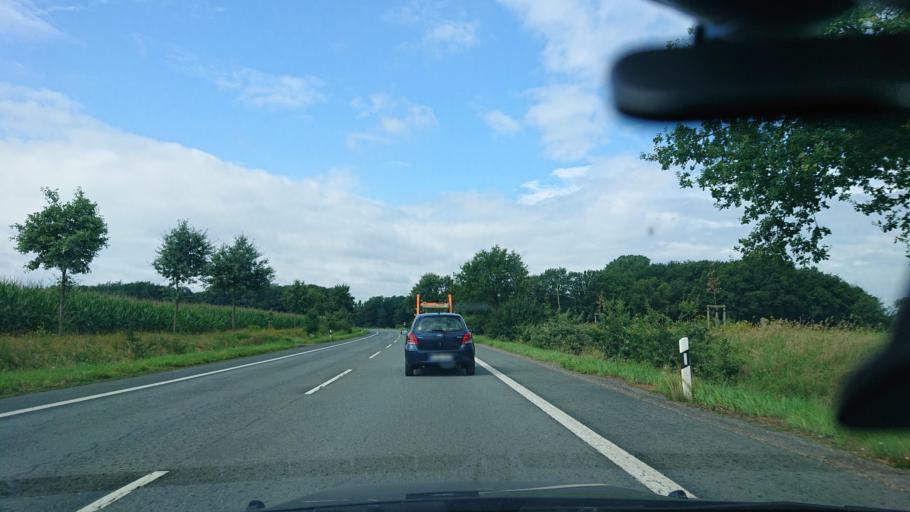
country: DE
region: North Rhine-Westphalia
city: Lunen
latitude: 51.6285
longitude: 7.5779
